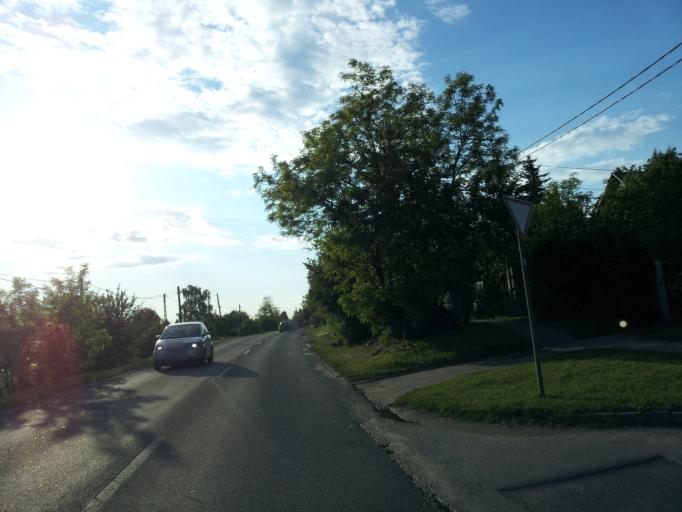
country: HU
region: Pest
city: Solymar
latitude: 47.5986
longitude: 18.9236
